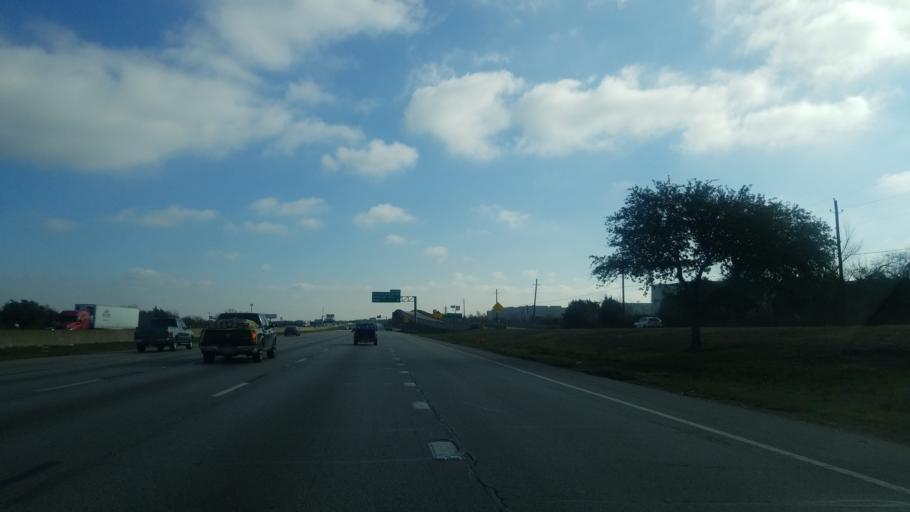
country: US
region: Texas
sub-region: Dallas County
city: DeSoto
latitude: 32.6421
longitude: -96.8138
